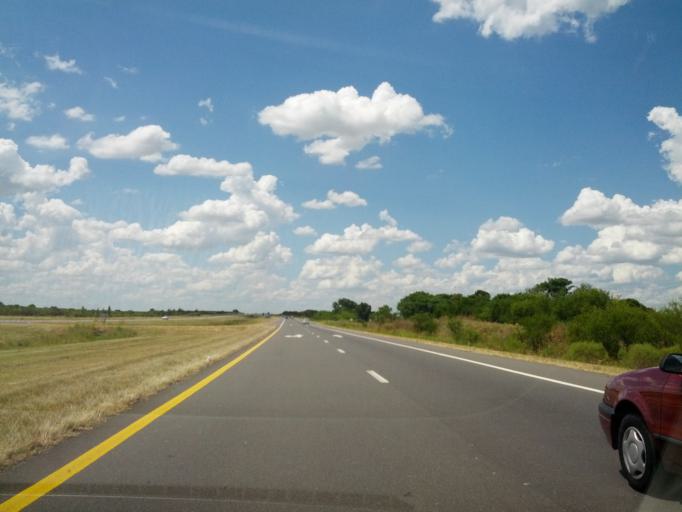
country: AR
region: Entre Rios
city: Colonia Elia
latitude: -32.7473
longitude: -58.4802
